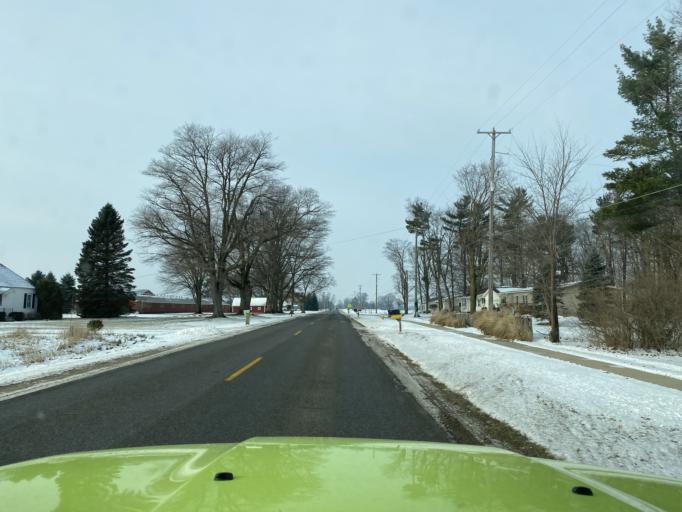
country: US
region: Michigan
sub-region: Ottawa County
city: Allendale
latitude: 42.9578
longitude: -85.9565
